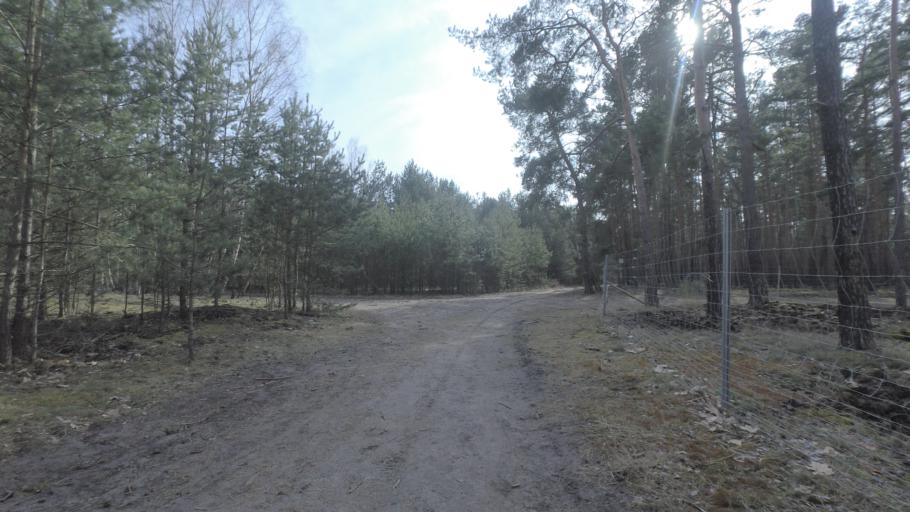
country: DE
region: Brandenburg
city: Ludwigsfelde
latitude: 52.3057
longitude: 13.2260
